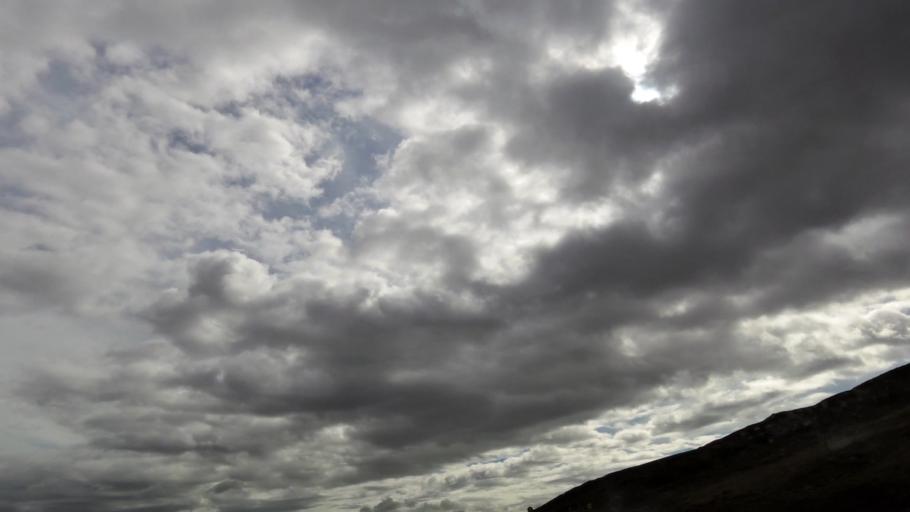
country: IS
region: West
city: Stykkisholmur
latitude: 65.5863
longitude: -22.1536
